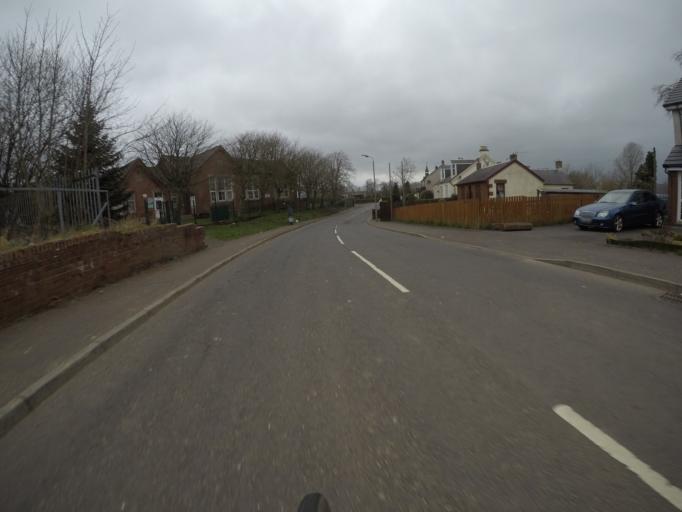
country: GB
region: Scotland
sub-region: North Ayrshire
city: Springside
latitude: 55.6153
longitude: -4.5894
